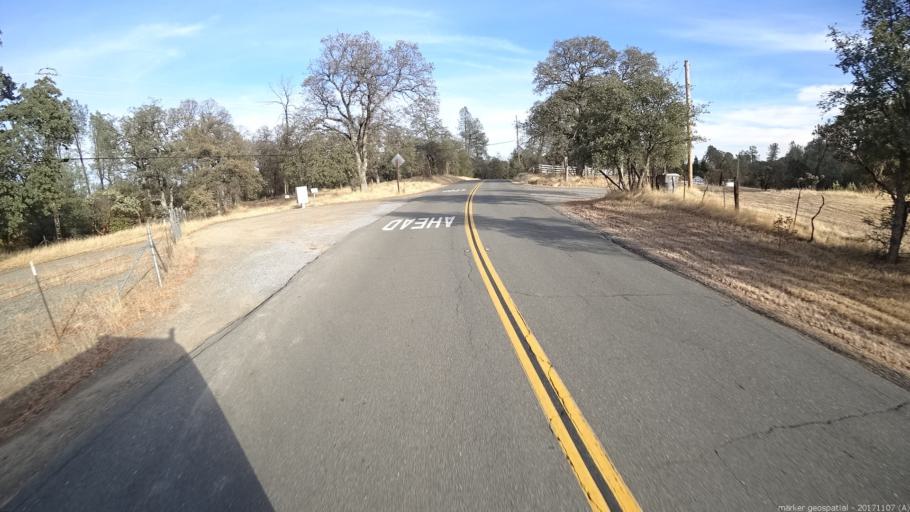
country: US
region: California
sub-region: Shasta County
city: Shasta
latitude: 40.5190
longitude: -122.4791
